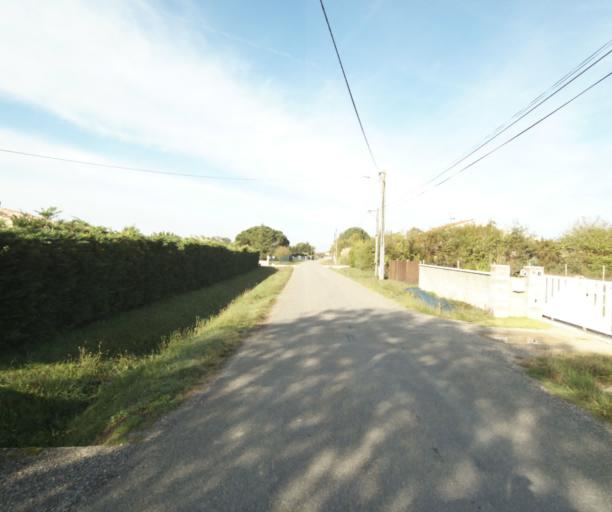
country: FR
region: Midi-Pyrenees
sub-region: Departement du Tarn-et-Garonne
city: Nohic
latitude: 43.9109
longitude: 1.4451
